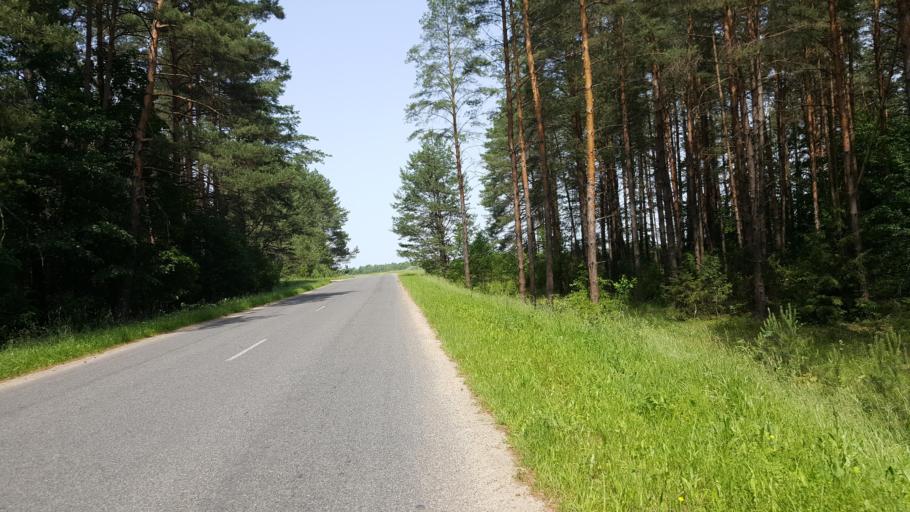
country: BY
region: Brest
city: Kamyanyuki
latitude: 52.5137
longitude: 23.8528
